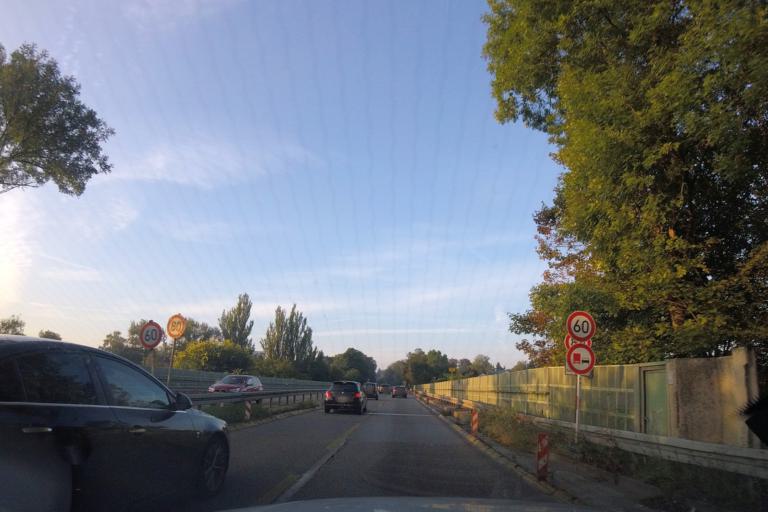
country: DE
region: Baden-Wuerttemberg
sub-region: Regierungsbezirk Stuttgart
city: Kornwestheim
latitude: 48.8639
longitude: 9.1966
